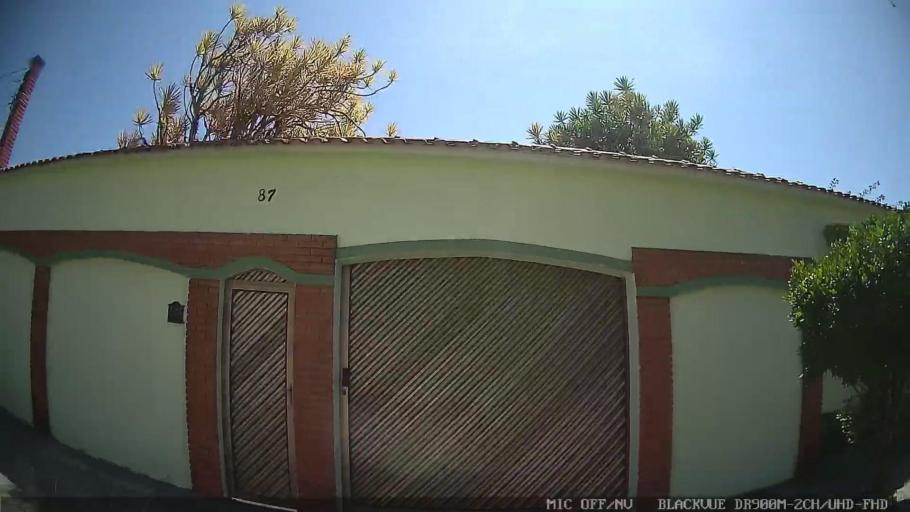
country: BR
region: Sao Paulo
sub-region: Peruibe
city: Peruibe
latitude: -24.3011
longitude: -46.9724
